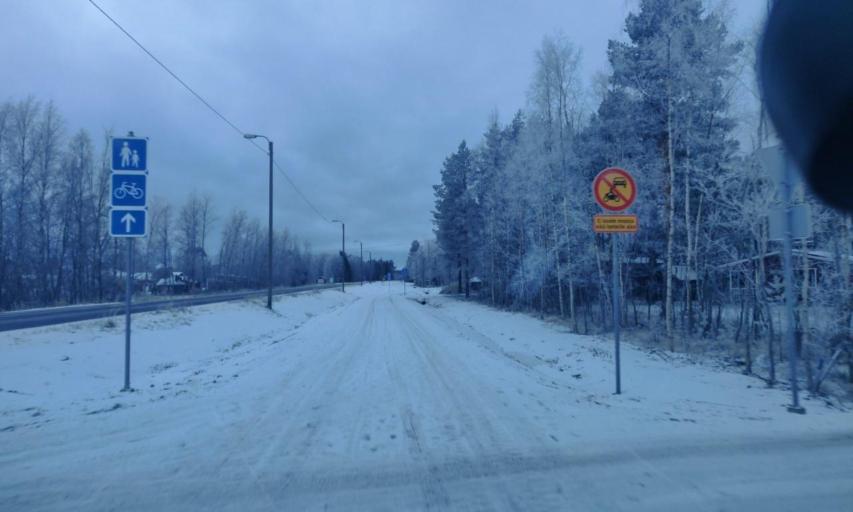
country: FI
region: Northern Ostrobothnia
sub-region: Oulu
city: Oulunsalo
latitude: 64.9837
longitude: 25.2681
